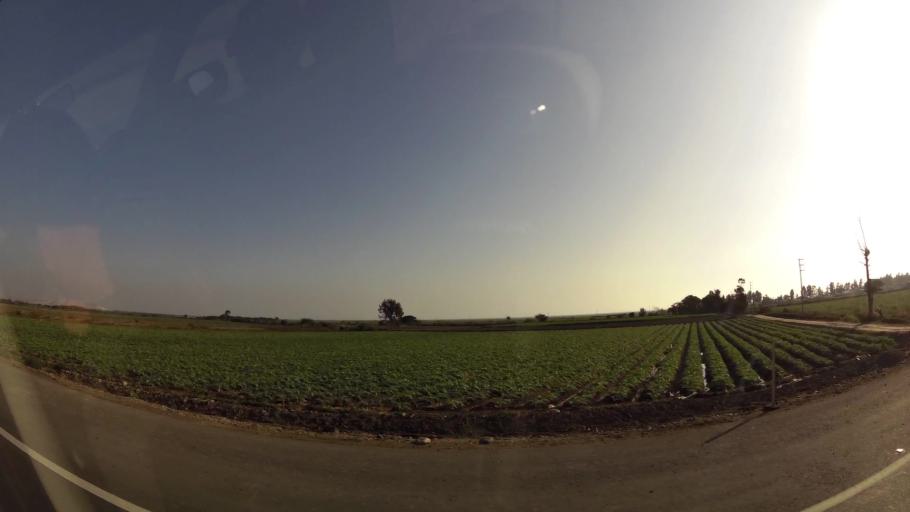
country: PE
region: Ica
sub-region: Provincia de Pisco
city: San Clemente
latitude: -13.5743
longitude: -76.1750
